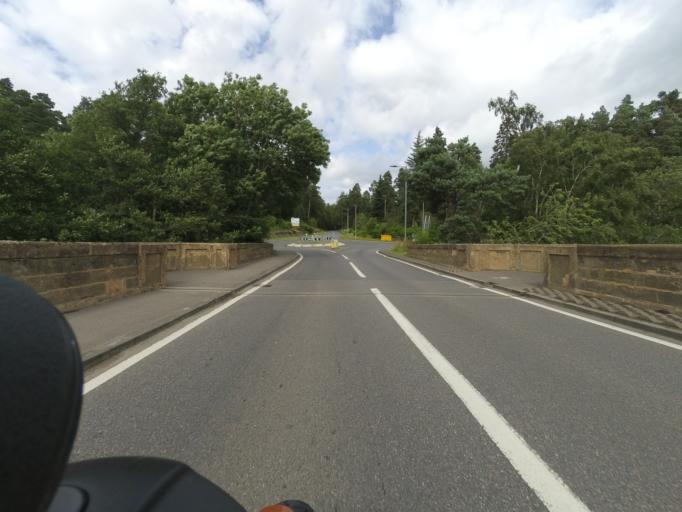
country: GB
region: Scotland
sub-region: Highland
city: Grantown on Spey
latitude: 57.3218
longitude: -3.6061
